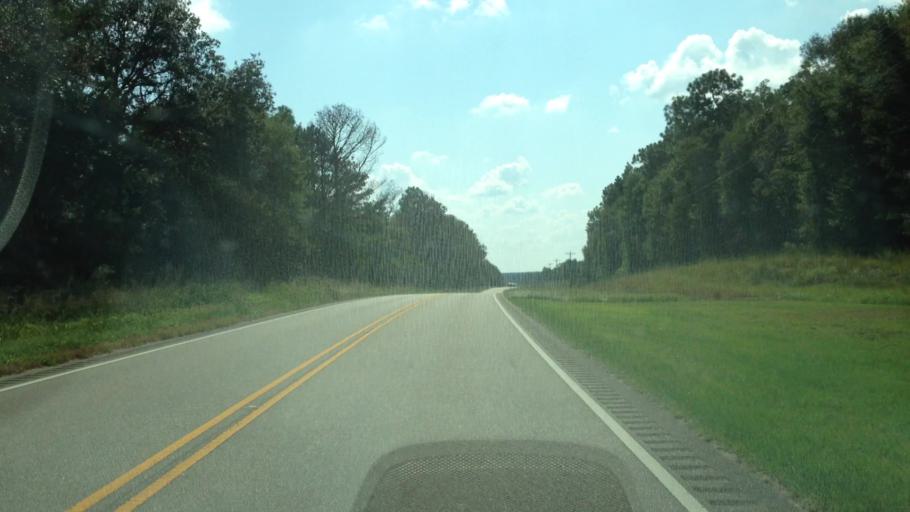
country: US
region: Alabama
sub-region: Covington County
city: Florala
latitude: 31.0504
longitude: -86.5829
